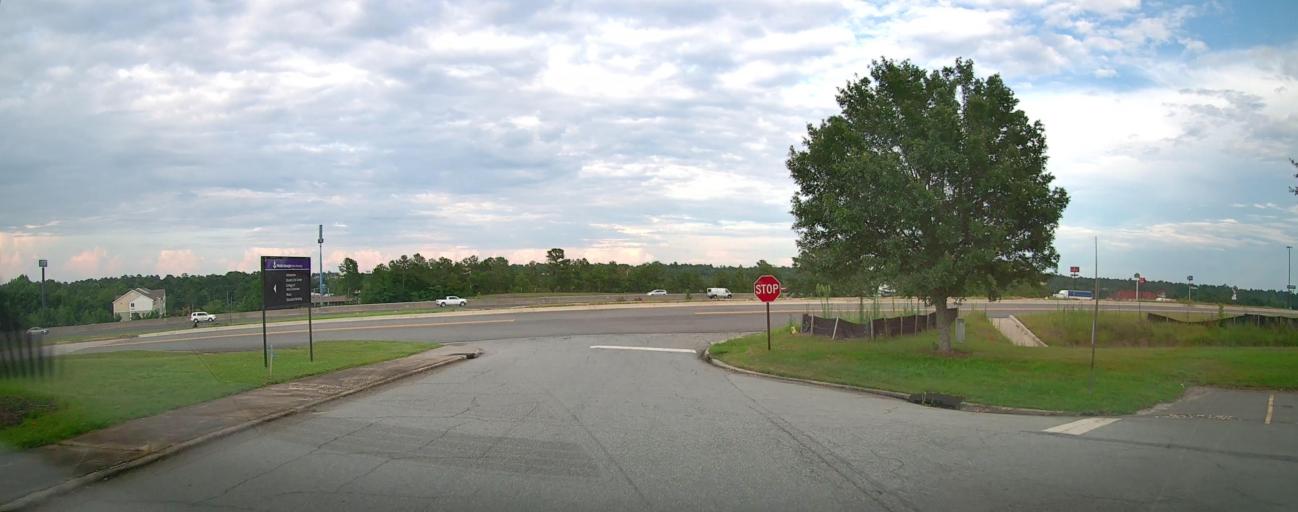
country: US
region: Georgia
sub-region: Bibb County
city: West Point
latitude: 32.8111
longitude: -83.7287
